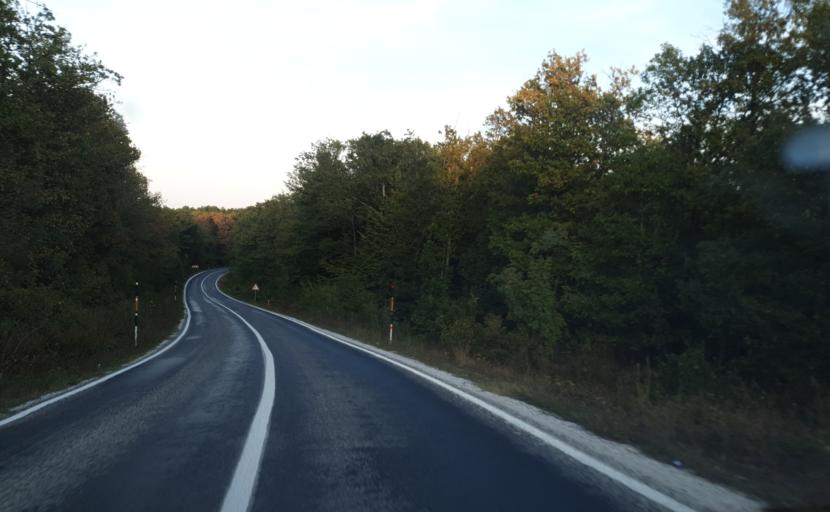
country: TR
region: Kirklareli
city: Igneada
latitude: 41.8670
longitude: 27.8410
